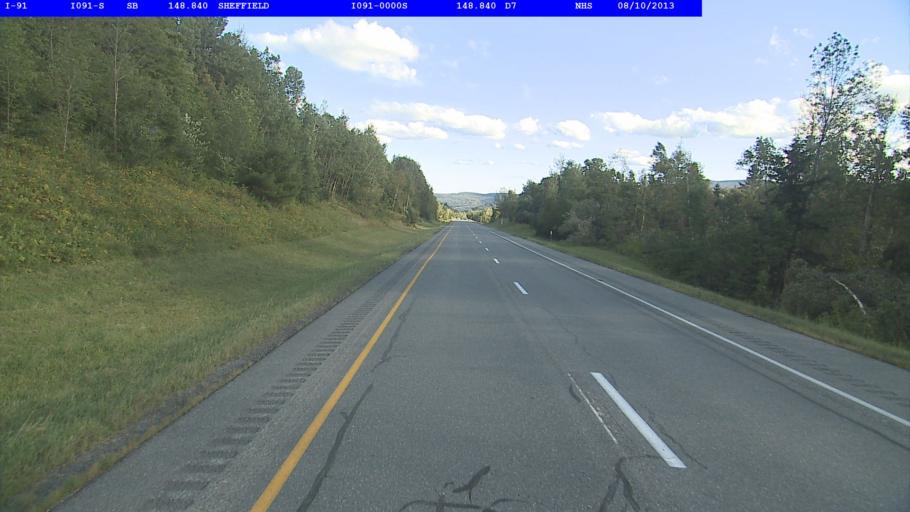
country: US
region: Vermont
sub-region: Caledonia County
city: Lyndonville
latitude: 44.6479
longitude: -72.1336
